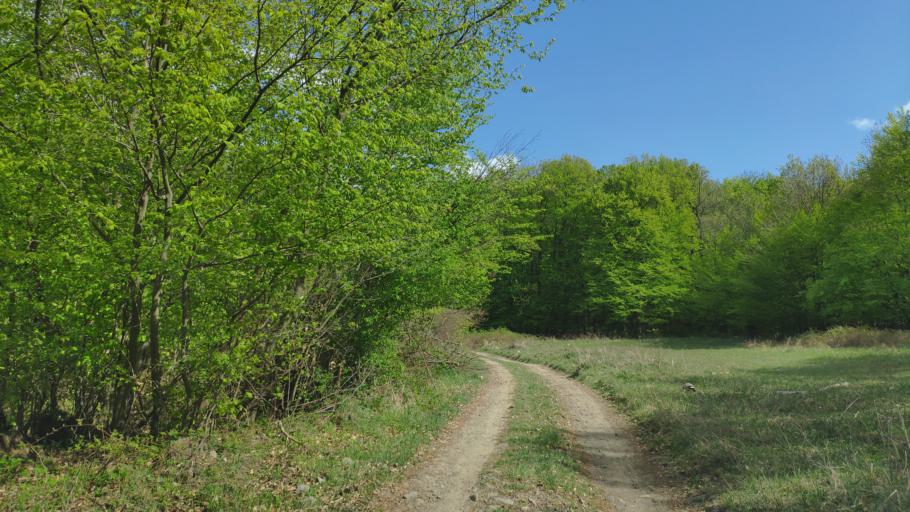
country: SK
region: Kosicky
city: Kosice
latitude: 48.6590
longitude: 21.4438
